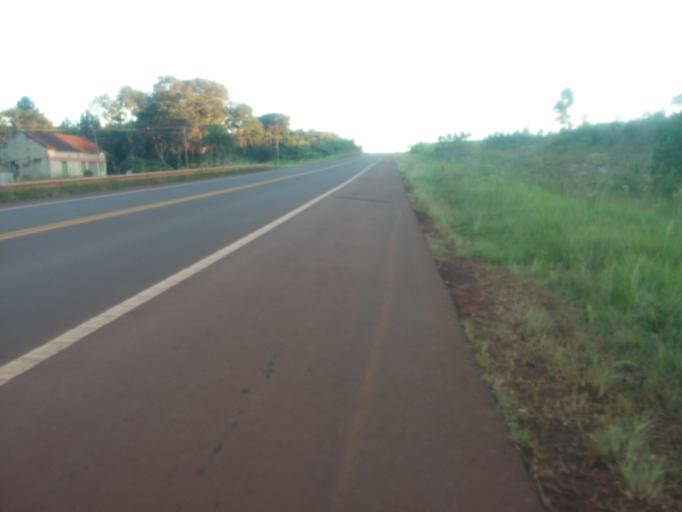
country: AR
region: Misiones
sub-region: Departamento de Obera
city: Obera
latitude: -27.4385
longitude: -55.0829
